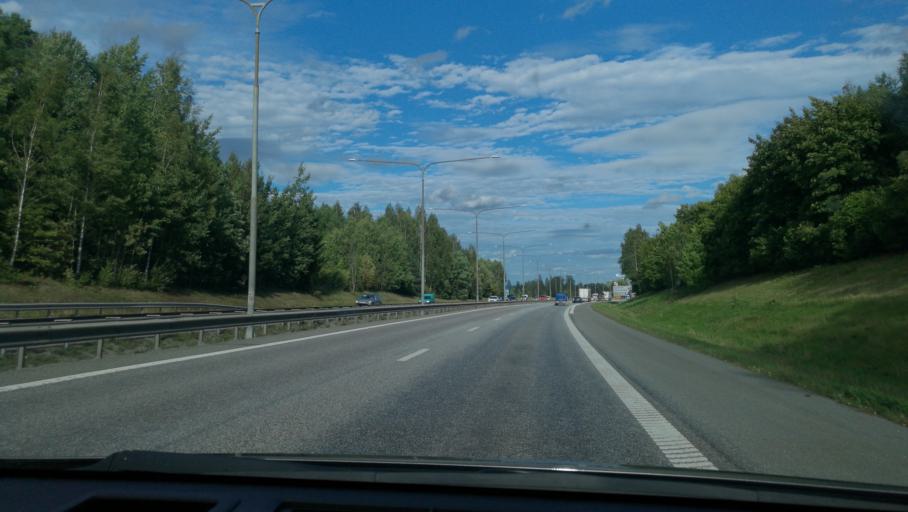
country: SE
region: OErebro
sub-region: Orebro Kommun
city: Orebro
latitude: 59.2921
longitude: 15.1934
